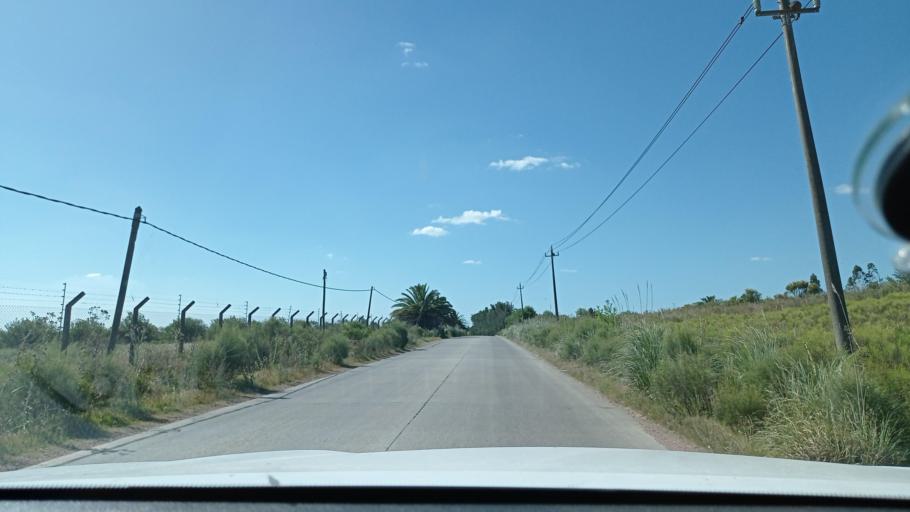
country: UY
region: Canelones
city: La Paz
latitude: -34.7803
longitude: -56.2551
